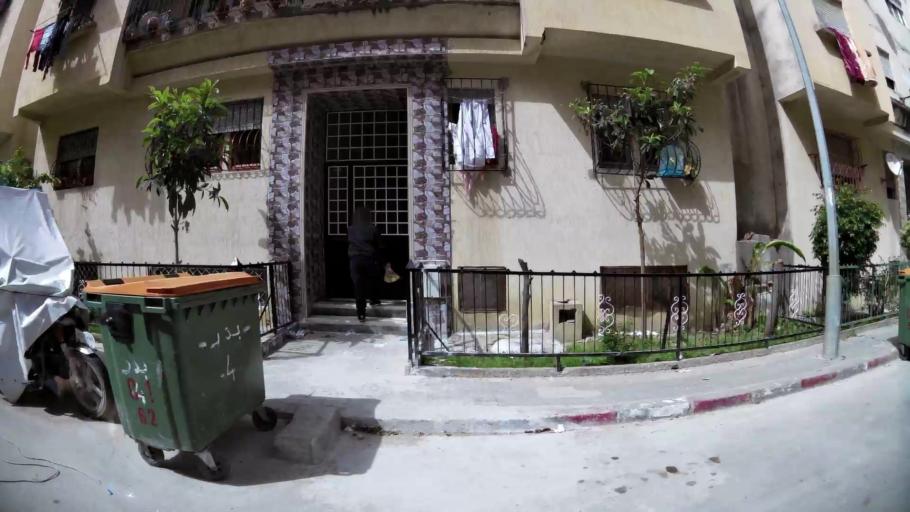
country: MA
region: Tanger-Tetouan
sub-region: Tanger-Assilah
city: Boukhalef
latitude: 35.7367
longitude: -5.8551
